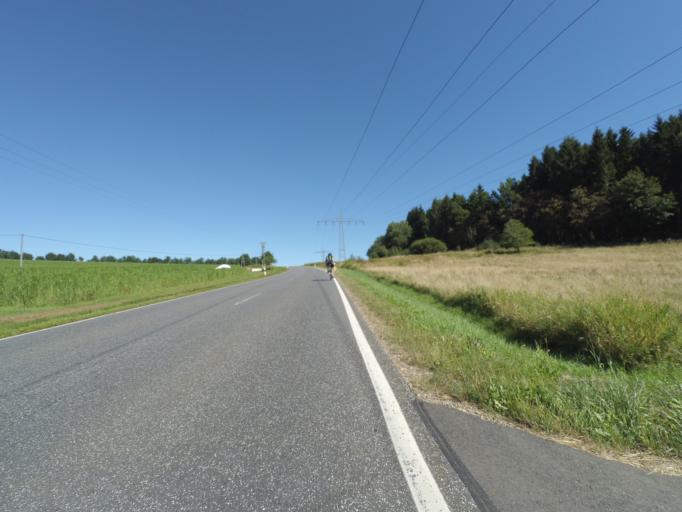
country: DE
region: Rheinland-Pfalz
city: Berlingen
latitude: 50.2308
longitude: 6.7247
